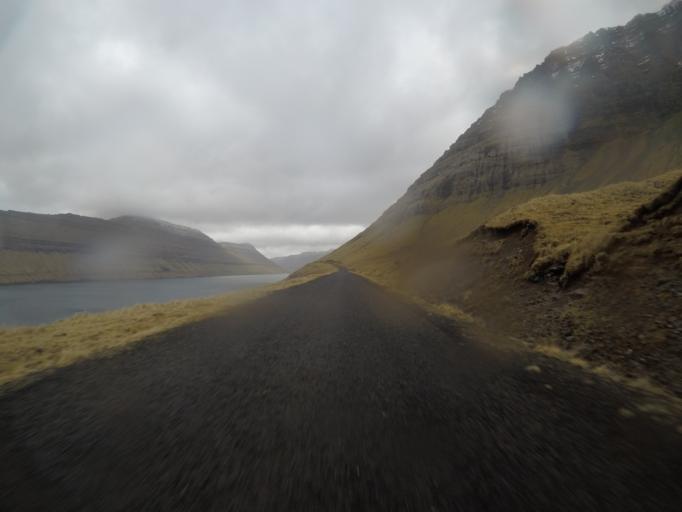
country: FO
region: Nordoyar
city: Klaksvik
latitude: 62.3345
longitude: -6.5767
